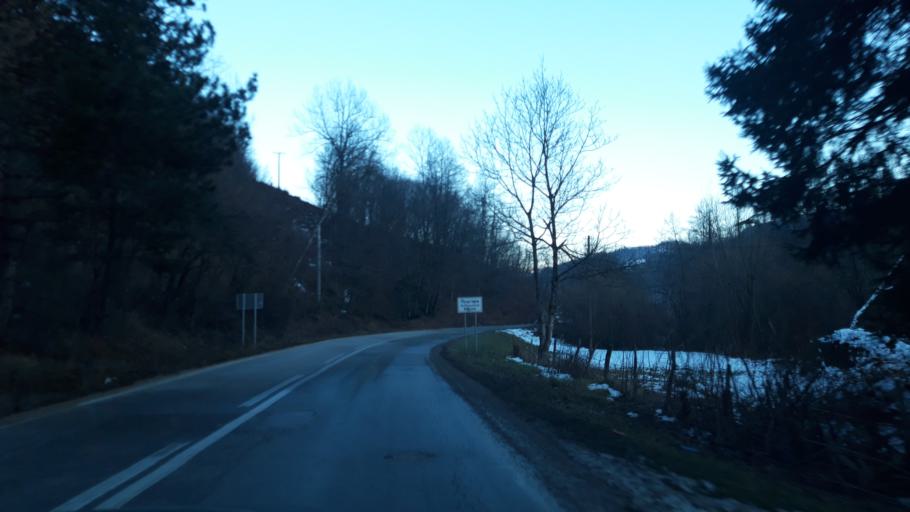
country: BA
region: Republika Srpska
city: Milici
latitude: 44.1655
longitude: 19.0399
